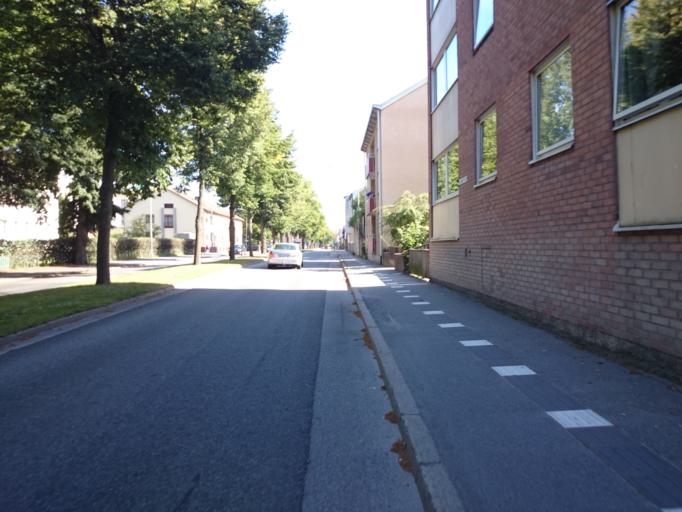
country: SE
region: Blekinge
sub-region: Karlshamns Kommun
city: Karlshamn
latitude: 56.1723
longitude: 14.8674
